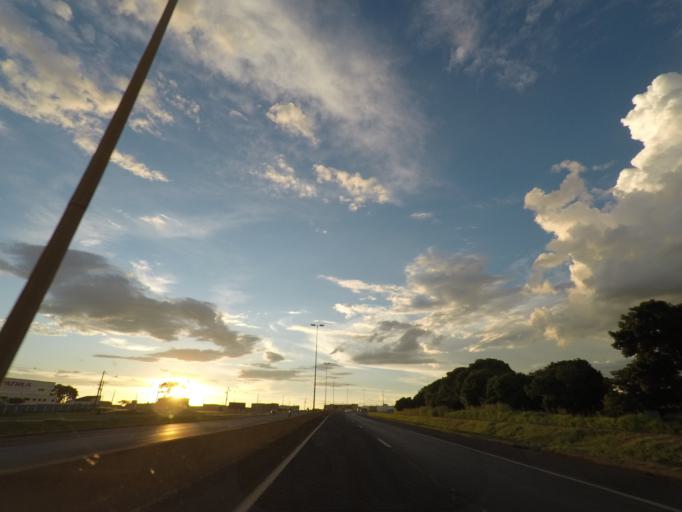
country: BR
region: Minas Gerais
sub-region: Uberaba
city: Uberaba
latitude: -19.7793
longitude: -47.9665
